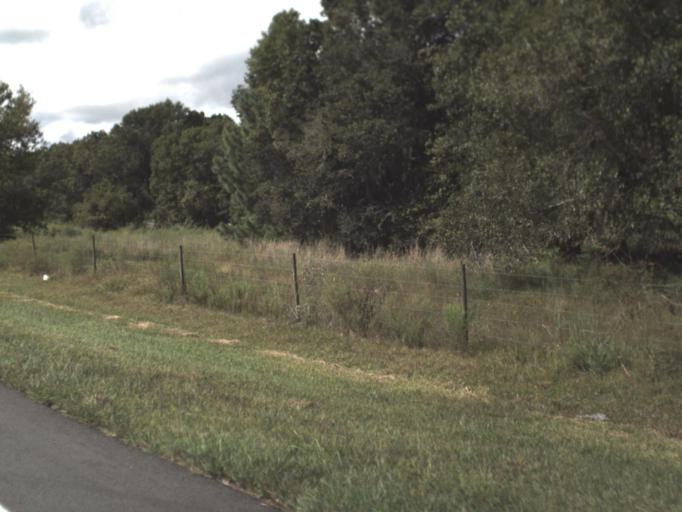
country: US
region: Florida
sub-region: Polk County
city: Winston
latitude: 28.0016
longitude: -82.0185
